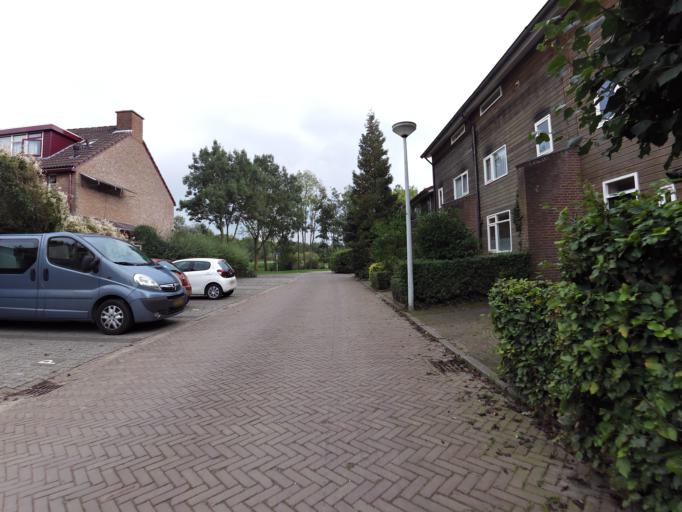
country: NL
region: Gelderland
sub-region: Gemeente Westervoort
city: Westervoort
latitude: 51.9525
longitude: 5.9839
